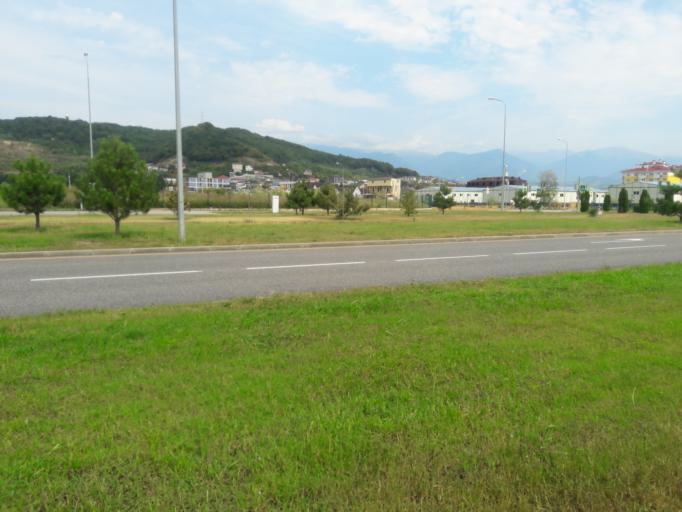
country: RU
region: Krasnodarskiy
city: Vysokoye
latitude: 43.4038
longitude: 39.9788
